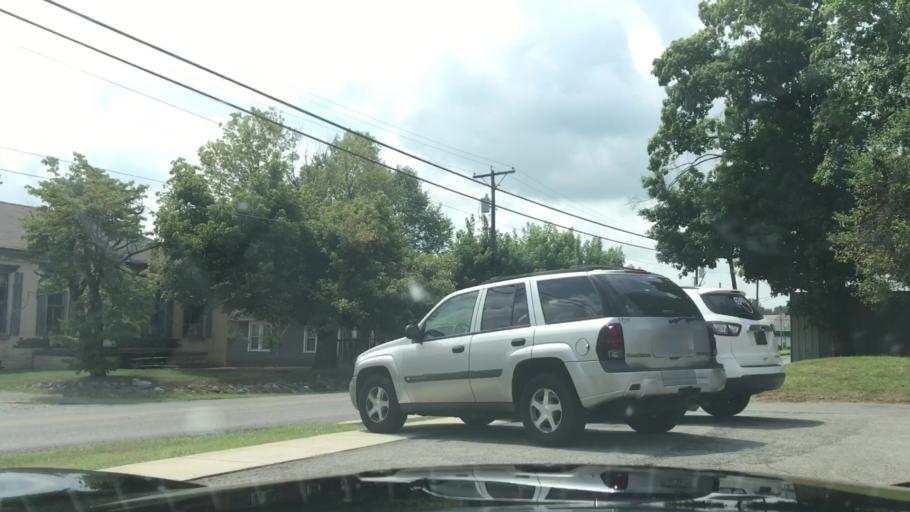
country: US
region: Kentucky
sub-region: Muhlenberg County
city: Greenville
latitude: 37.2160
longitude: -87.1796
